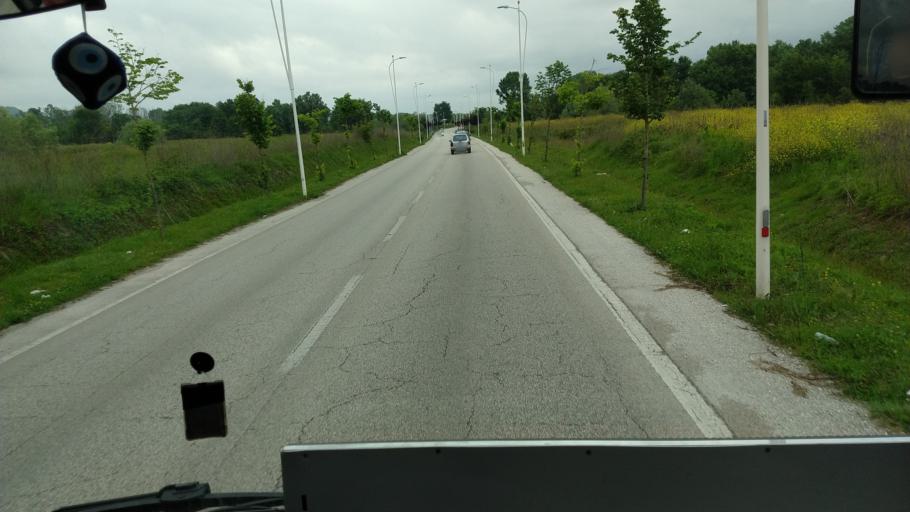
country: AL
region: Tirane
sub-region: Rrethi i Tiranes
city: Berxull
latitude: 41.4107
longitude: 19.7034
